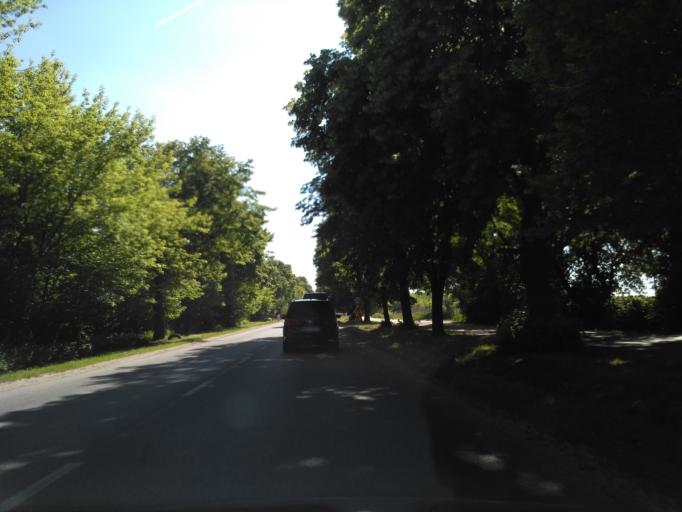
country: PL
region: Lublin Voivodeship
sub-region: Powiat lubelski
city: Lublin
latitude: 51.1996
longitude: 22.5546
